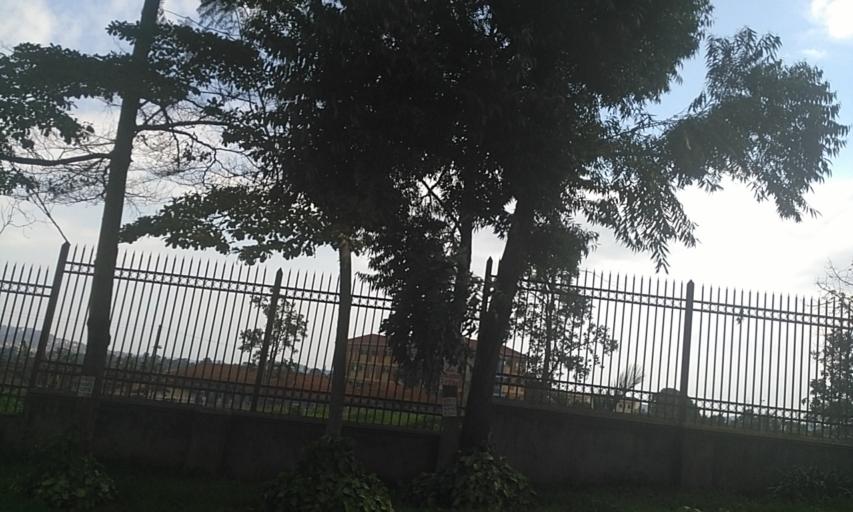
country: UG
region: Central Region
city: Kampala Central Division
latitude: 0.3144
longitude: 32.5625
